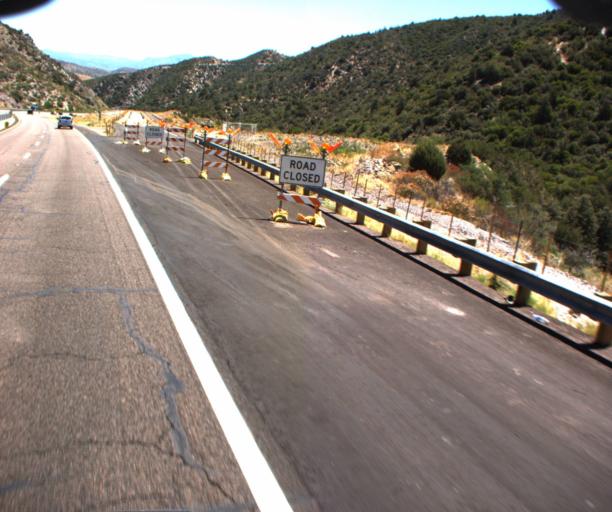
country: US
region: Arizona
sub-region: Gila County
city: Tonto Basin
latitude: 33.9478
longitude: -111.4225
